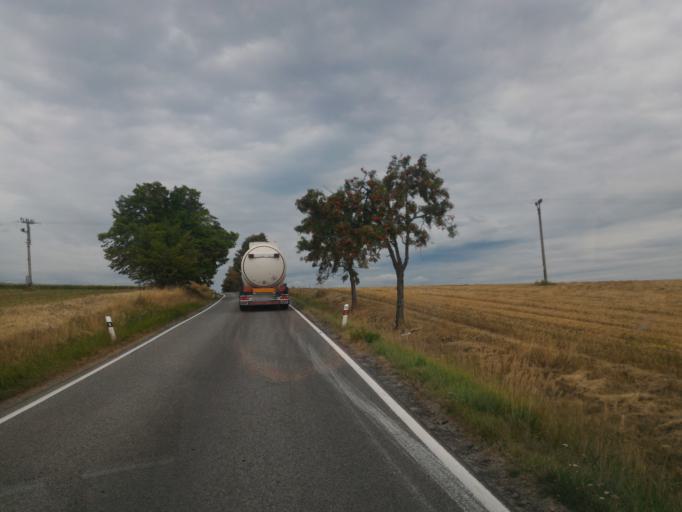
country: CZ
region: Vysocina
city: Zeletava
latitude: 49.1837
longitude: 15.5972
